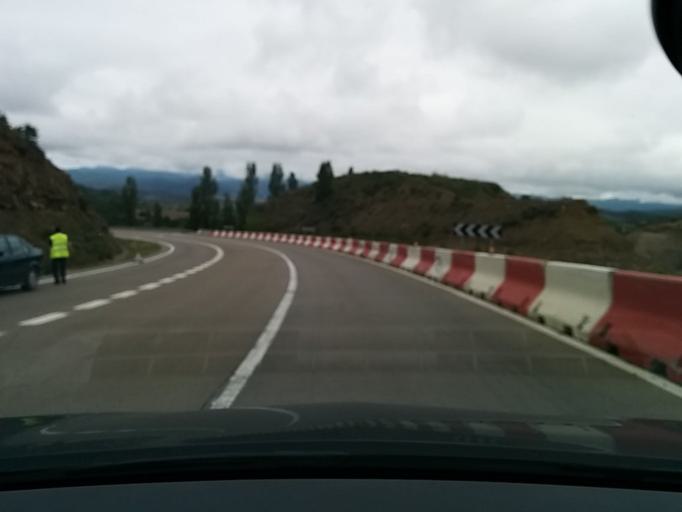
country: ES
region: Aragon
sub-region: Provincia de Huesca
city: Arguis
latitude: 42.3956
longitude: -0.3716
